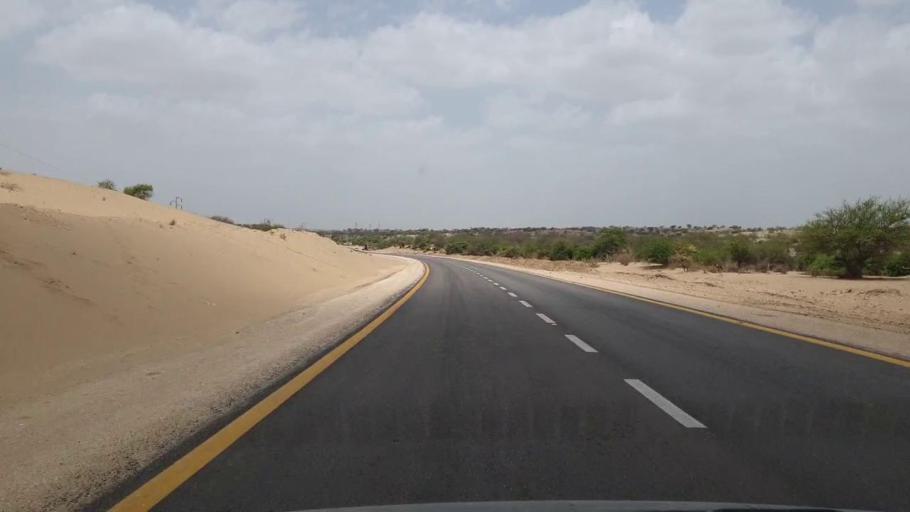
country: PK
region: Sindh
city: Naukot
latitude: 24.8457
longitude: 69.5716
